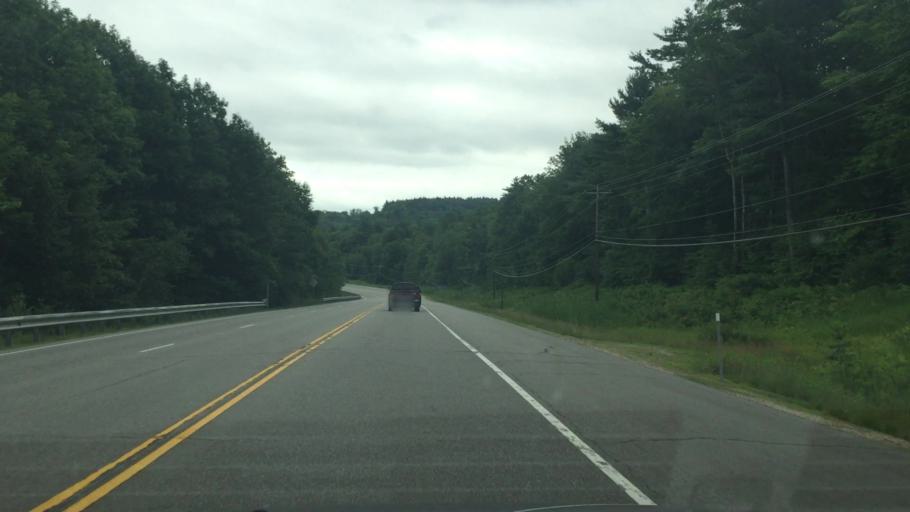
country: US
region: New Hampshire
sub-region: Belknap County
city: Meredith
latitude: 43.6419
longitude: -71.5164
